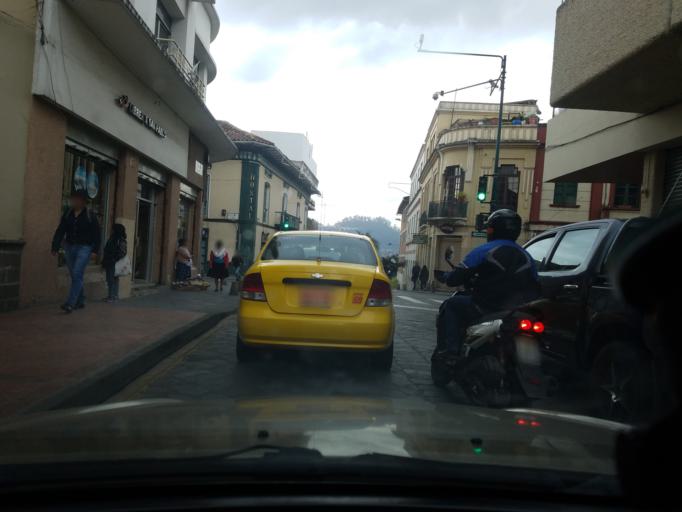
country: EC
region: Azuay
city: Cuenca
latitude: -2.9006
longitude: -79.0055
